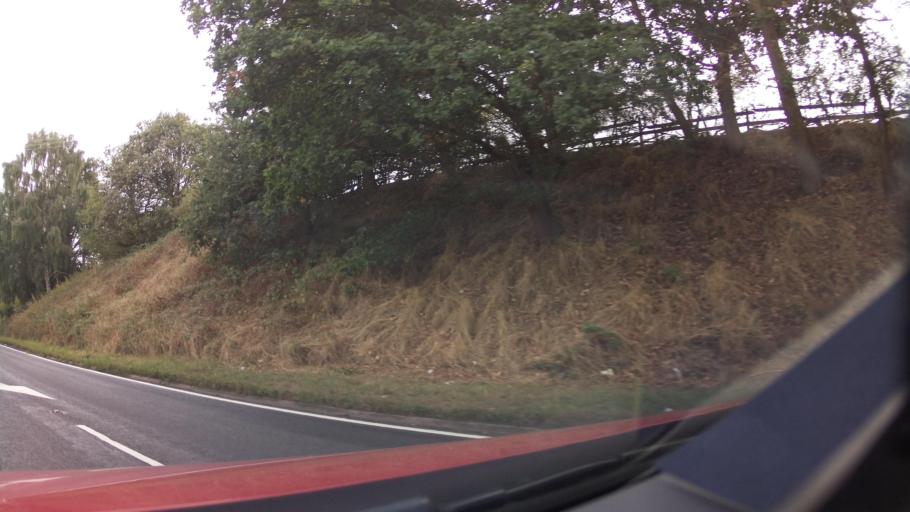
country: GB
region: England
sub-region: Shropshire
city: Bridgnorth
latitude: 52.5685
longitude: -2.3928
